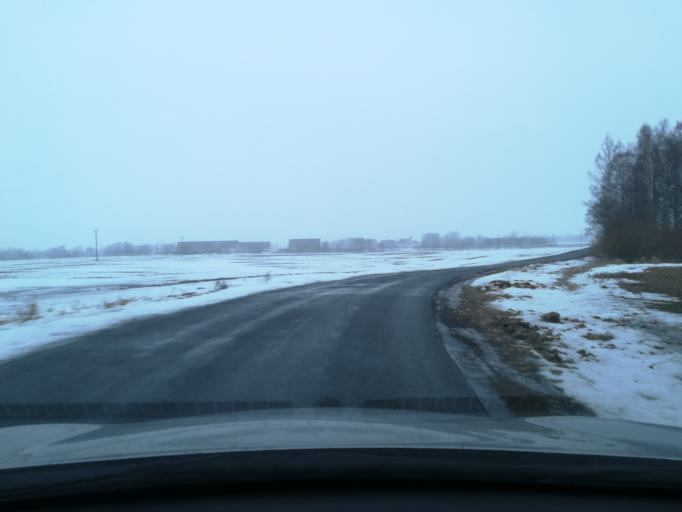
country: EE
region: Harju
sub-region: Raasiku vald
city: Raasiku
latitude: 59.3515
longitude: 25.2063
